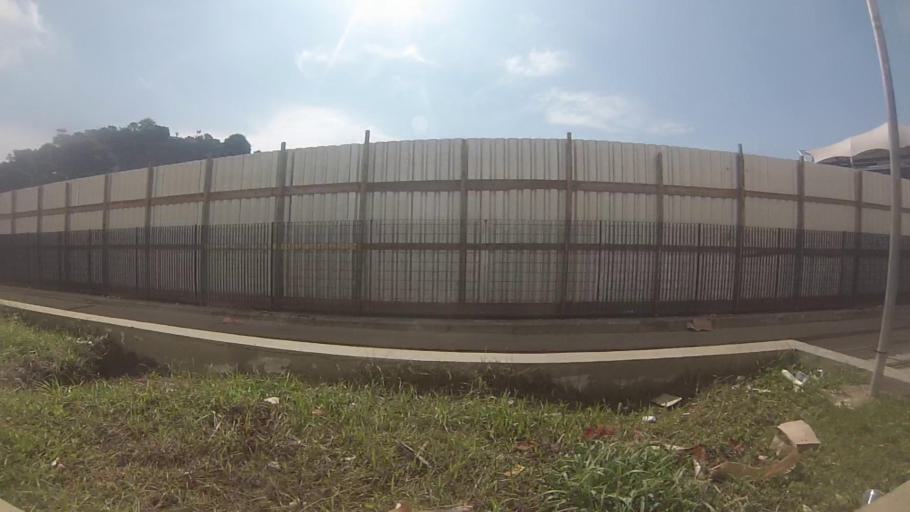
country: BR
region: Rio de Janeiro
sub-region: Rio De Janeiro
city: Rio de Janeiro
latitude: -22.9031
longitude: -43.1932
